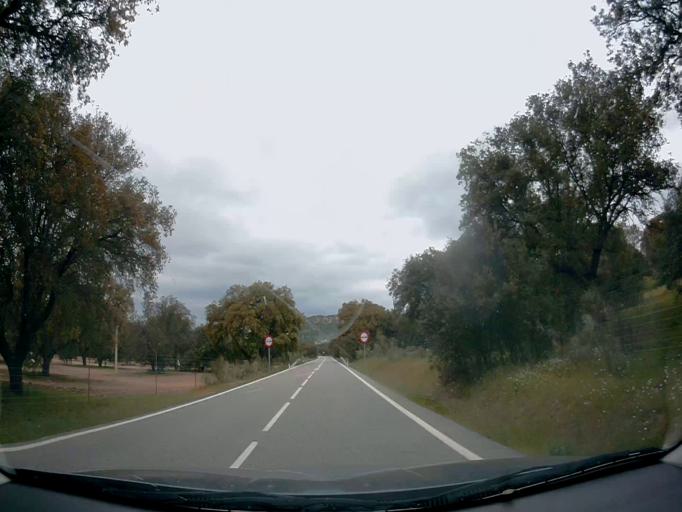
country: ES
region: Madrid
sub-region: Provincia de Madrid
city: Quijorna
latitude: 40.4241
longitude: -4.0922
